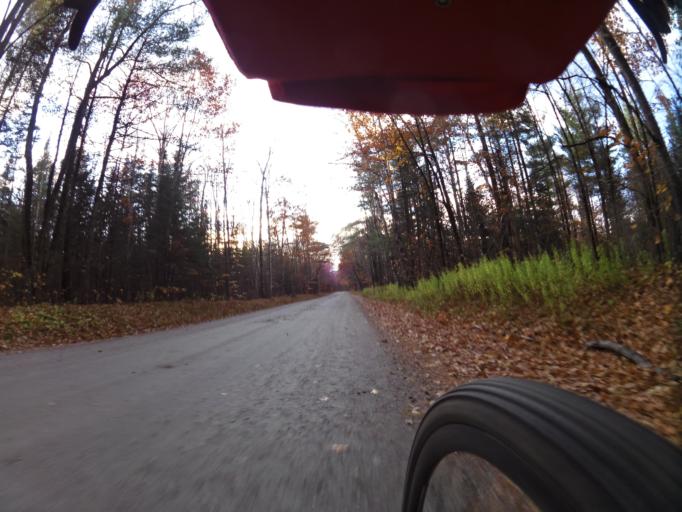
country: CA
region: Quebec
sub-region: Outaouais
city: Shawville
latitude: 45.6619
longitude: -76.3045
